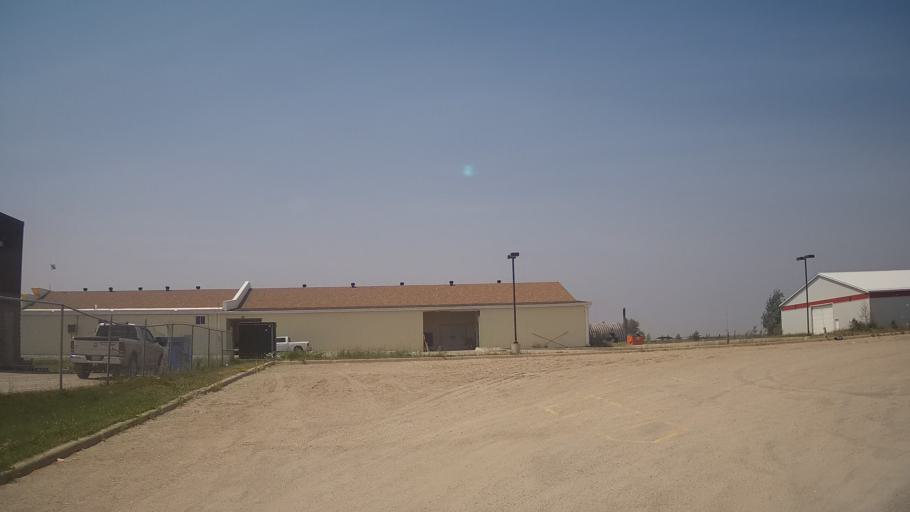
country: CA
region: Ontario
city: Timmins
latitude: 48.4738
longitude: -81.3947
